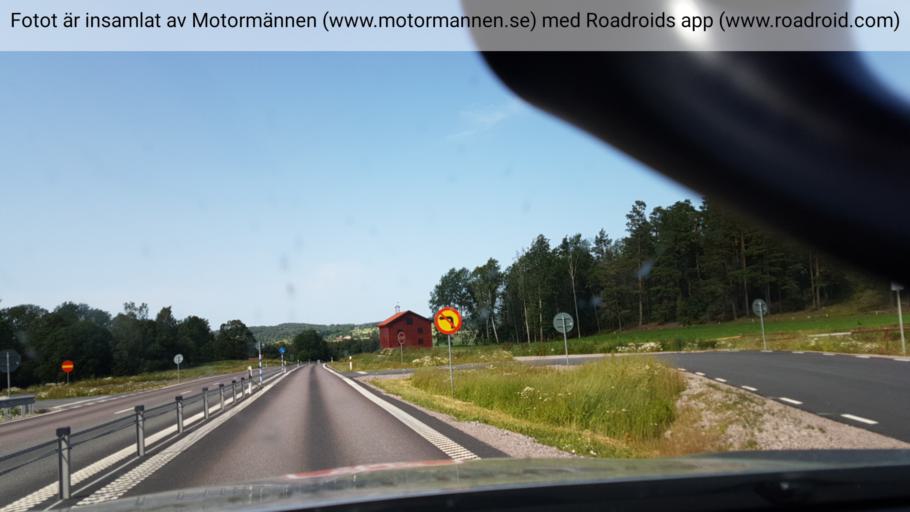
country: SE
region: Joenkoeping
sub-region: Tranas Kommun
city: Tranas
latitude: 57.9751
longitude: 14.9139
